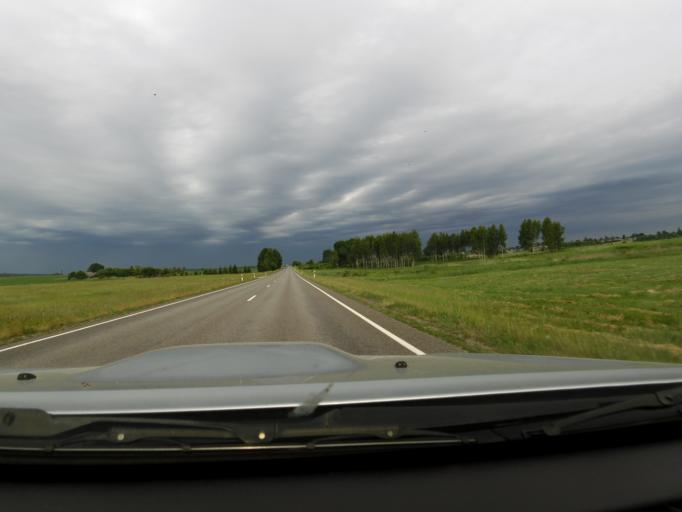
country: LT
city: Jieznas
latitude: 54.5787
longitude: 24.3366
